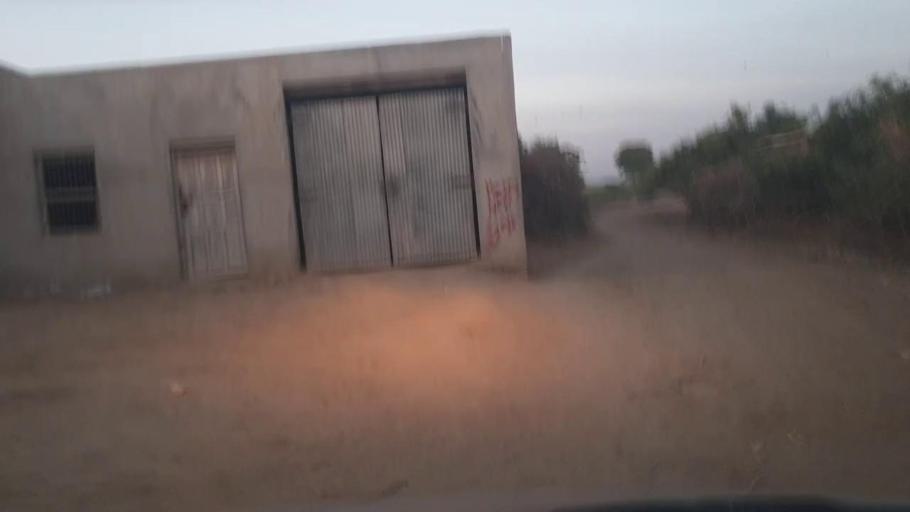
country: PK
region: Sindh
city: Kunri
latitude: 25.2258
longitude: 69.5254
